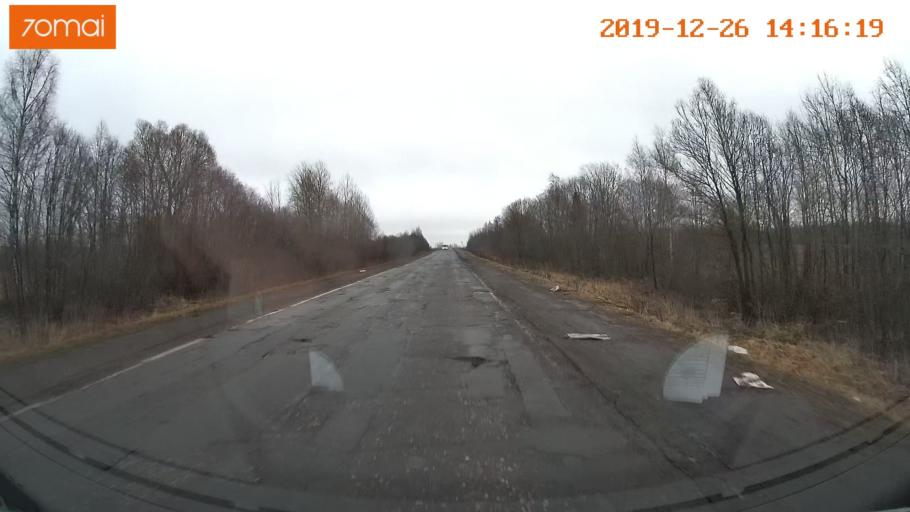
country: RU
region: Jaroslavl
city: Poshekhon'ye
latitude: 58.5168
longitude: 39.0613
